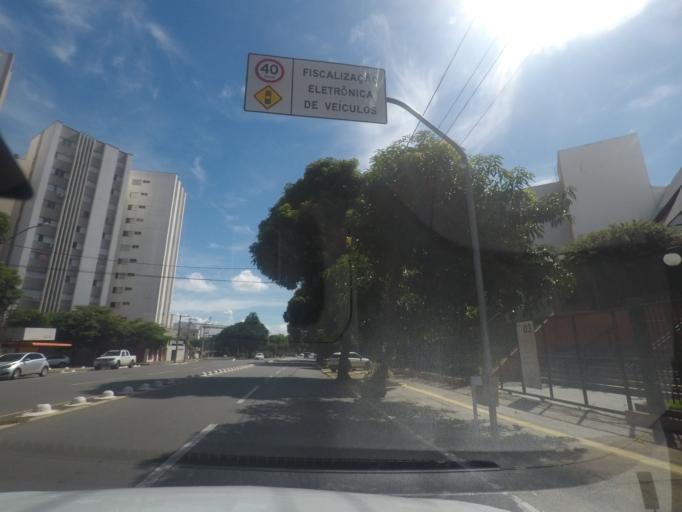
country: BR
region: Goias
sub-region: Goiania
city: Goiania
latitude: -16.6747
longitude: -49.2650
